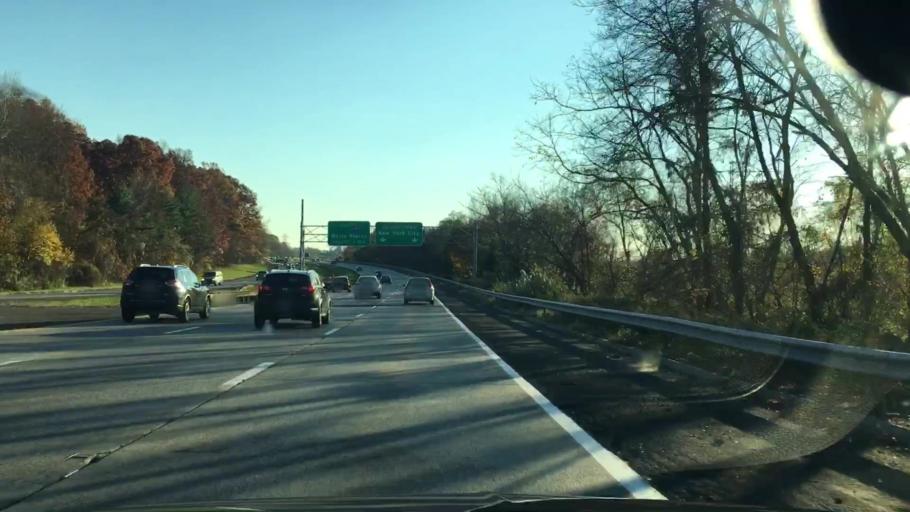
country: US
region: New York
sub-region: Westchester County
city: Elmsford
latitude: 41.0678
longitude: -73.8051
